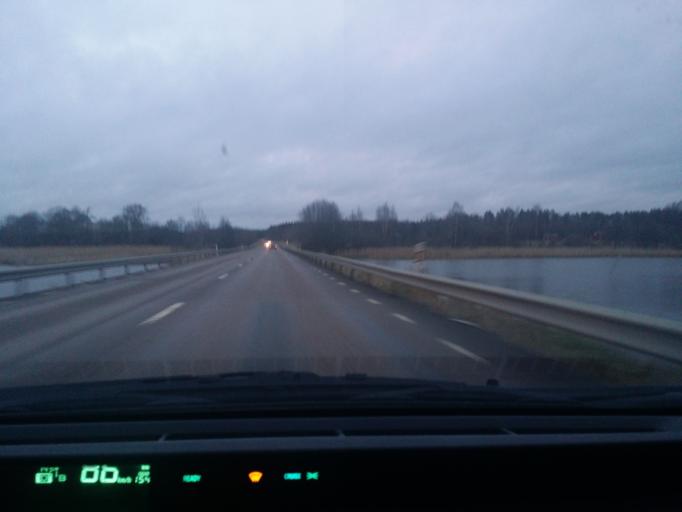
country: SE
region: Soedermanland
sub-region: Eskilstuna Kommun
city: Kvicksund
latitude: 59.4803
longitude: 16.3050
